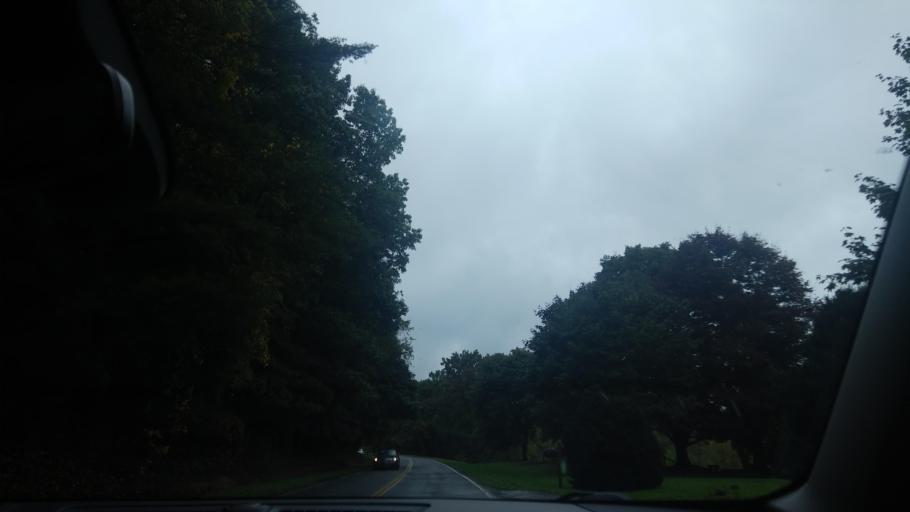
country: US
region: Virginia
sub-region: City of Galax
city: Galax
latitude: 36.6298
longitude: -80.9206
